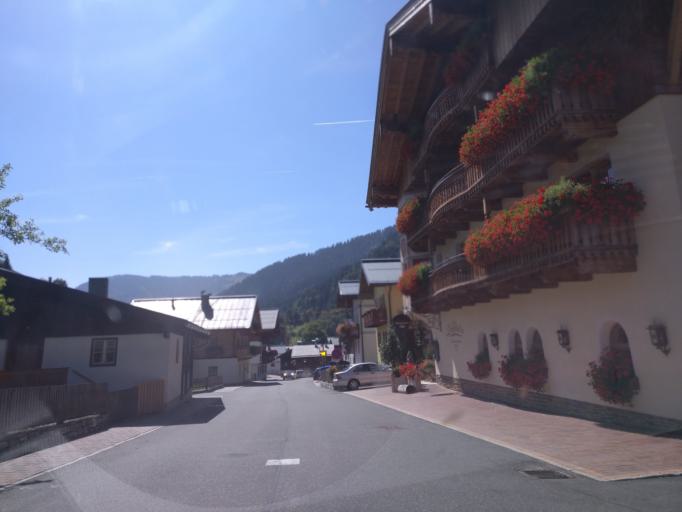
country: AT
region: Salzburg
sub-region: Politischer Bezirk Zell am See
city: Dienten am Hochkonig
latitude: 47.3835
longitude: 13.0039
